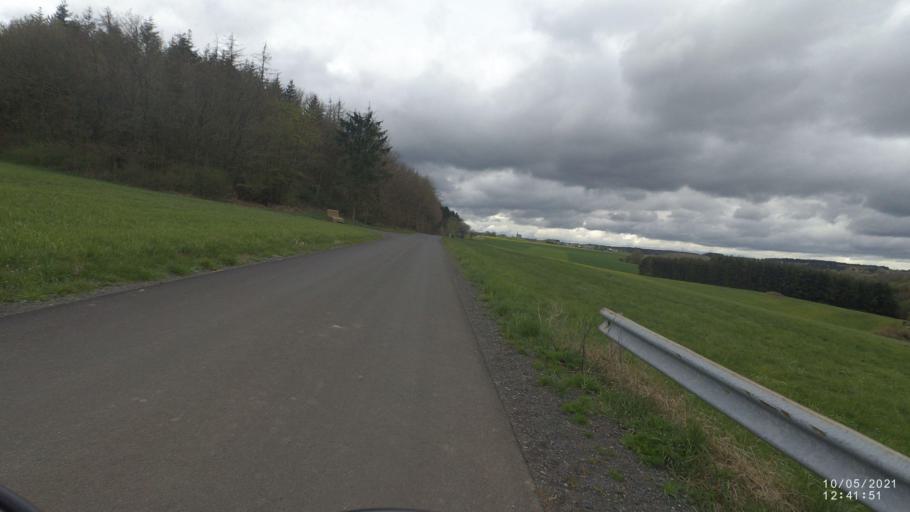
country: DE
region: Rheinland-Pfalz
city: Nachtsheim
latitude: 50.3158
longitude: 7.0841
